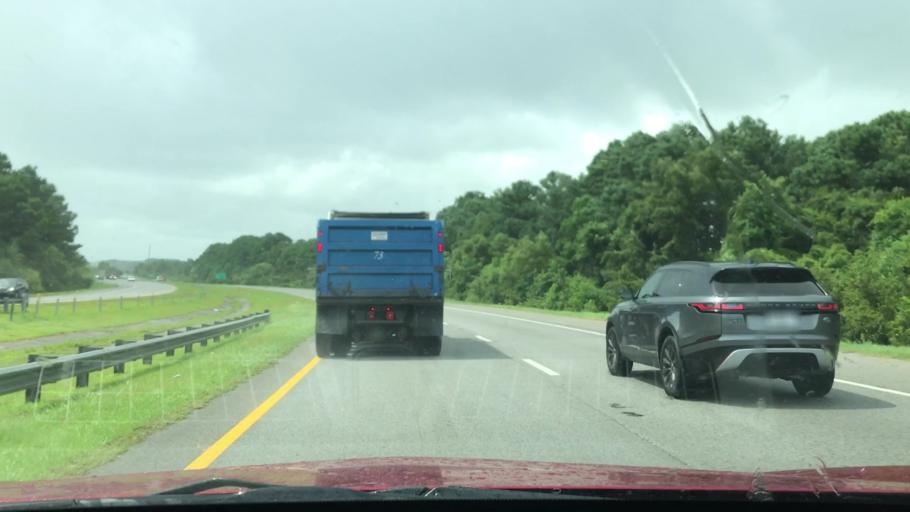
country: US
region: South Carolina
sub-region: Charleston County
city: Mount Pleasant
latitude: 32.8348
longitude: -79.8540
